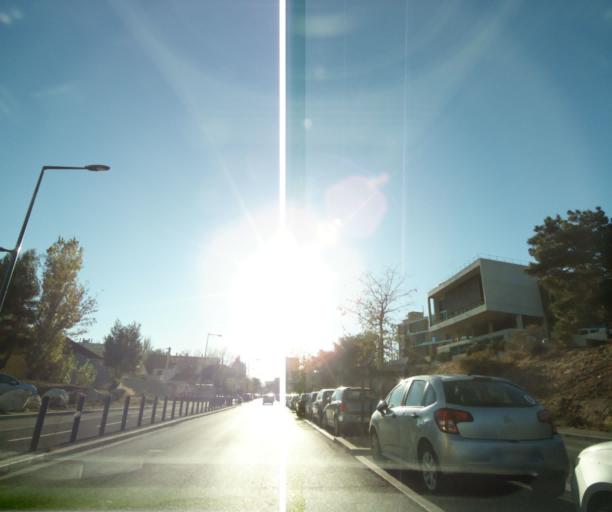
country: FR
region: Provence-Alpes-Cote d'Azur
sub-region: Departement des Bouches-du-Rhone
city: Marseille 13
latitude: 43.3346
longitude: 5.4324
